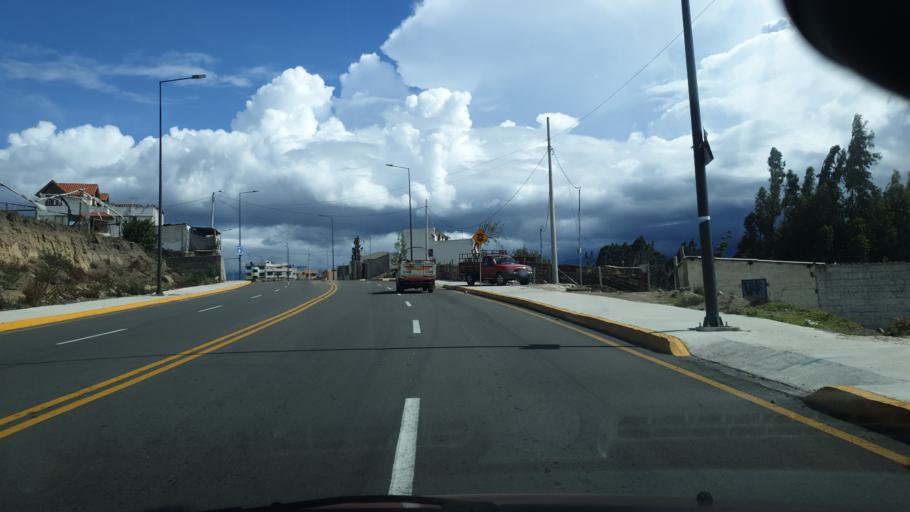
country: EC
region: Tungurahua
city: Ambato
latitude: -1.2938
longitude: -78.6308
